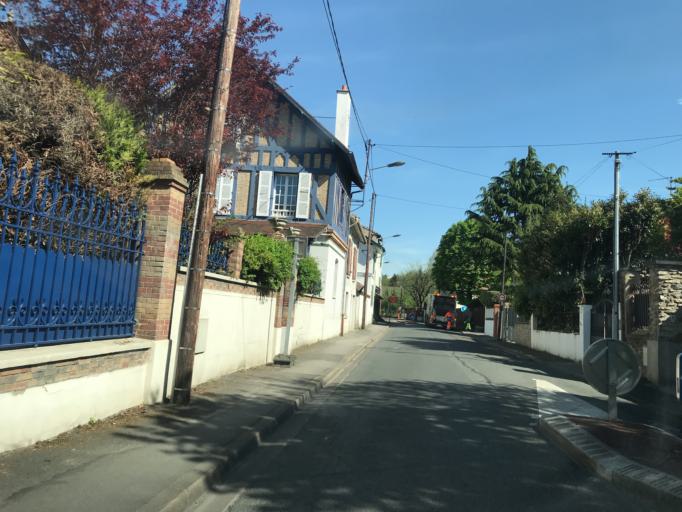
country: FR
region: Ile-de-France
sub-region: Departement du Val-de-Marne
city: Chennevieres-sur-Marne
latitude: 48.7948
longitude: 2.5243
